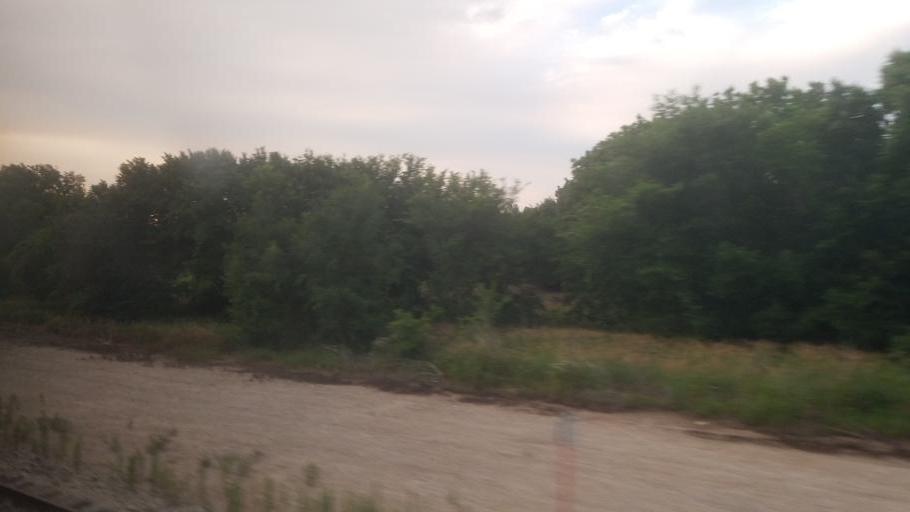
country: US
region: Kansas
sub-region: Marion County
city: Peabody
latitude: 38.1654
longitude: -97.1004
